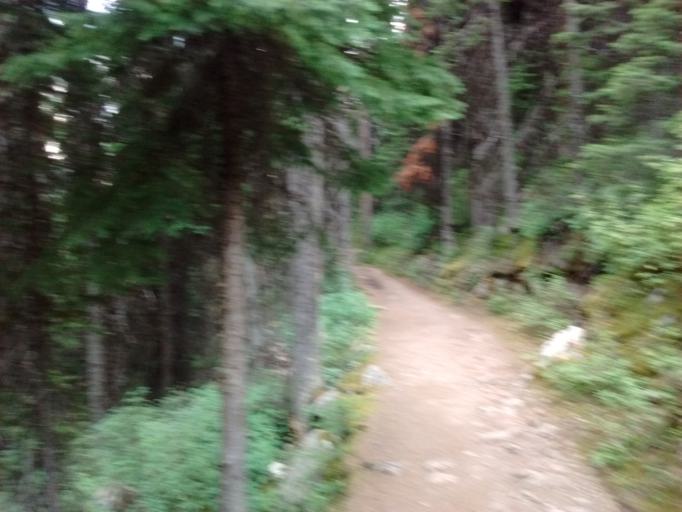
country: CA
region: Alberta
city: Lake Louise
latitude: 51.4138
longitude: -116.2416
